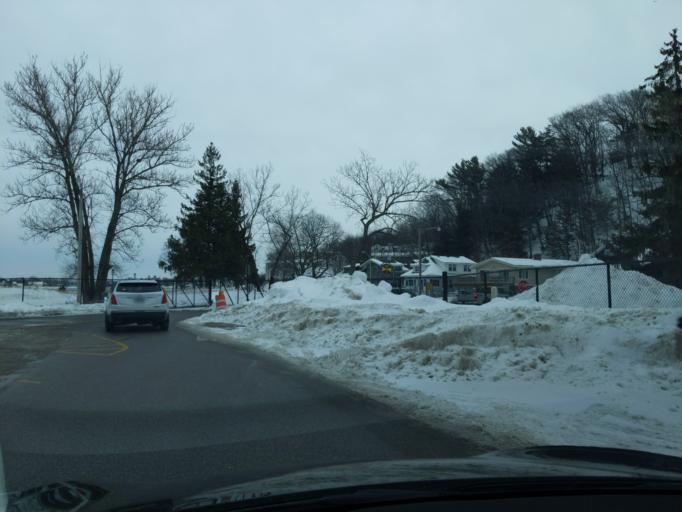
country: US
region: Michigan
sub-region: Ottawa County
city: Grand Haven
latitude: 43.0580
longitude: -86.2462
